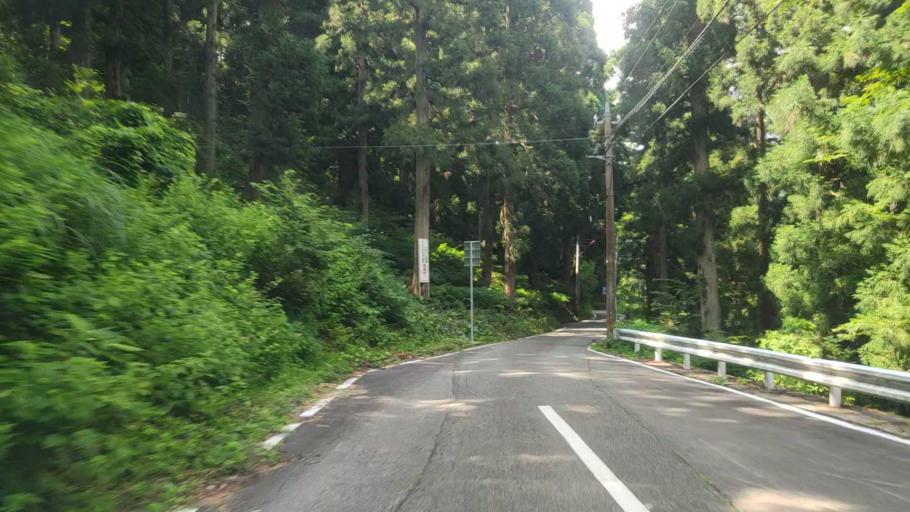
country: JP
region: Fukui
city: Katsuyama
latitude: 36.2105
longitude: 136.5281
